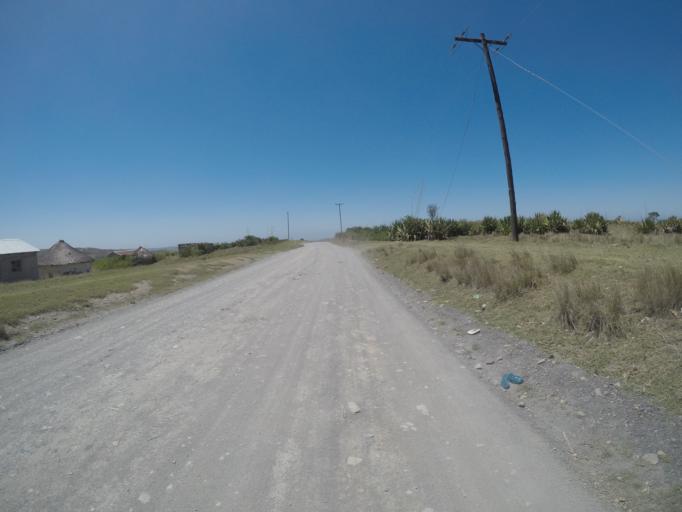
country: ZA
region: Eastern Cape
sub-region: OR Tambo District Municipality
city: Libode
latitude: -31.9832
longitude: 29.0381
